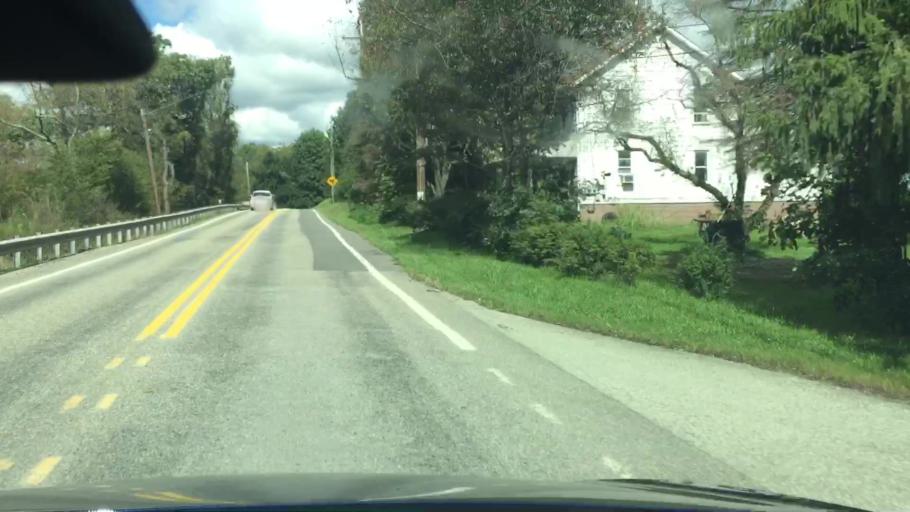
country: US
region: Pennsylvania
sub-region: Allegheny County
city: Russellton
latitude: 40.6266
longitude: -79.8327
